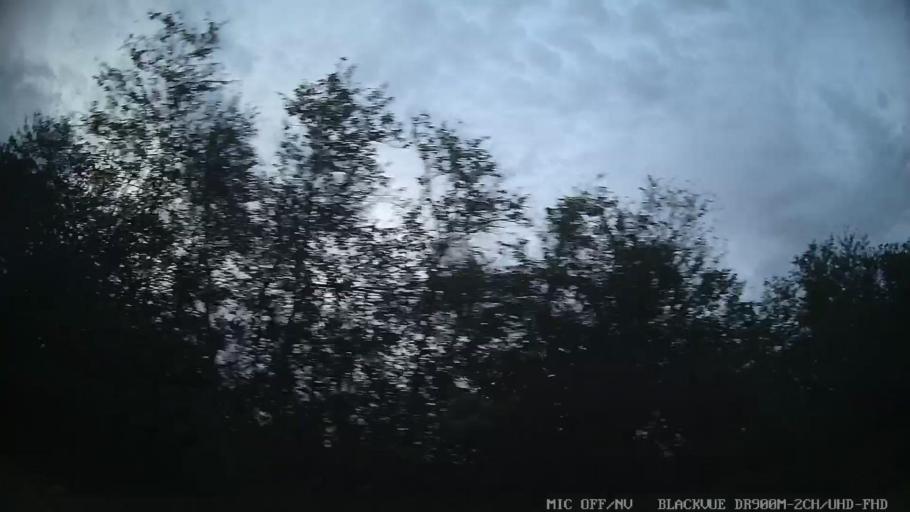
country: BR
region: Sao Paulo
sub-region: Amparo
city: Amparo
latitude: -22.8236
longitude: -46.7624
